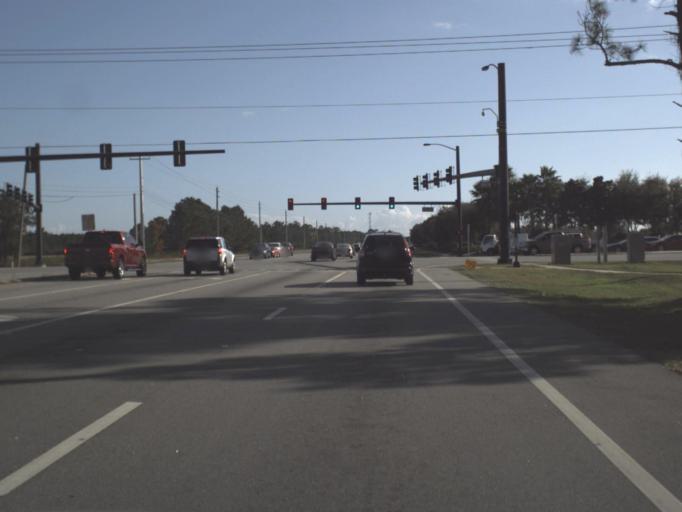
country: US
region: Florida
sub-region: Volusia County
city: Holly Hill
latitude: 29.2246
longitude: -81.0941
